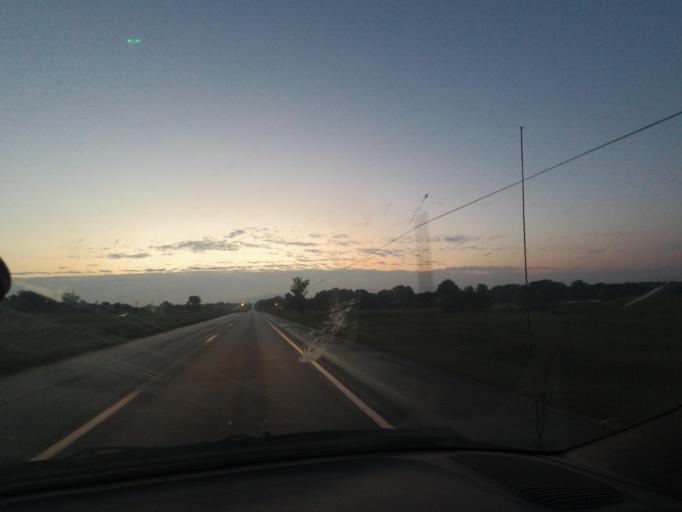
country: US
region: Missouri
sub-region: Linn County
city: Brookfield
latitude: 39.7791
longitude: -93.1313
